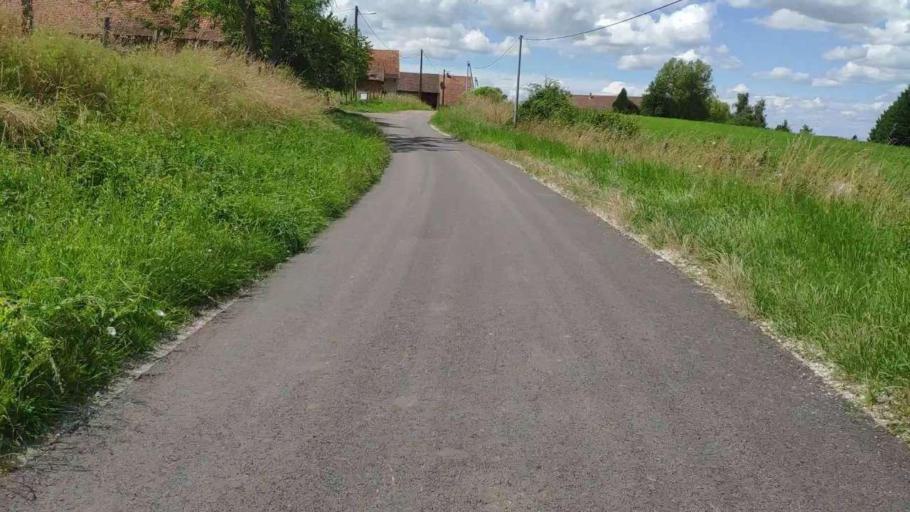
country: FR
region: Franche-Comte
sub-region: Departement du Jura
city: Chaussin
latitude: 46.8817
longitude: 5.4609
